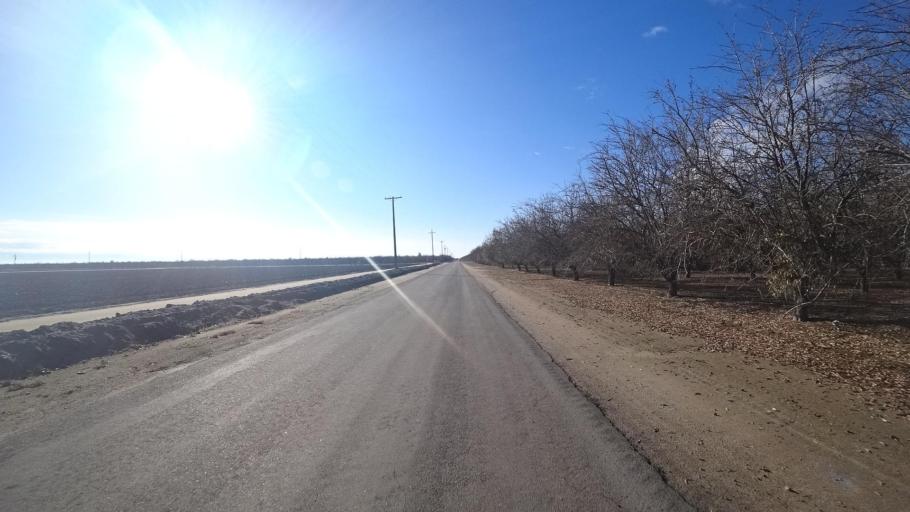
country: US
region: California
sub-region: Kern County
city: McFarland
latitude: 35.6978
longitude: -119.2942
